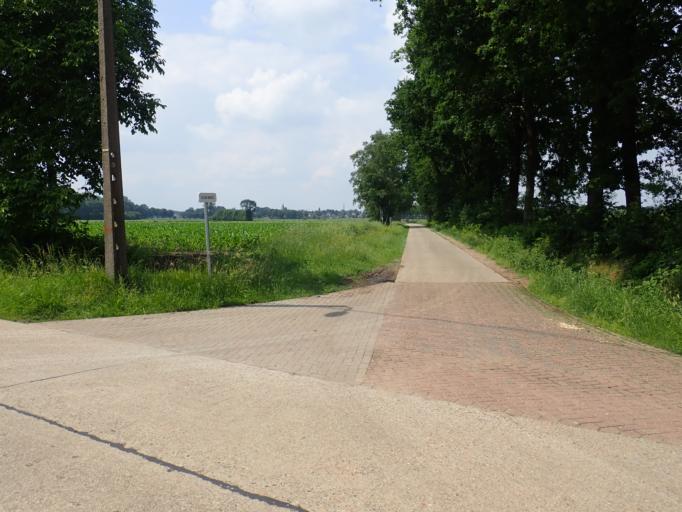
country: BE
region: Flanders
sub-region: Provincie Antwerpen
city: Kasterlee
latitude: 51.2357
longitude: 4.9164
